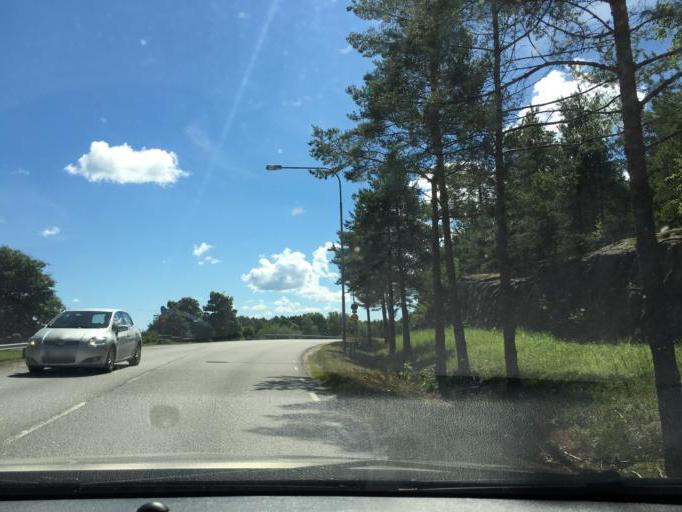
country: SE
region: Stockholm
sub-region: Nacka Kommun
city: Fisksatra
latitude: 59.2928
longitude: 18.2420
